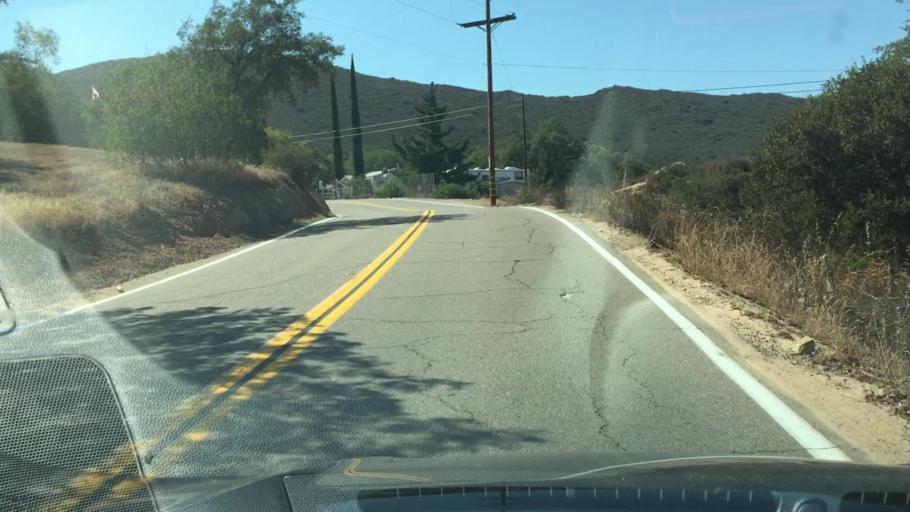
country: US
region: California
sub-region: San Diego County
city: Harbison Canyon
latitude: 32.7480
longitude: -116.7914
